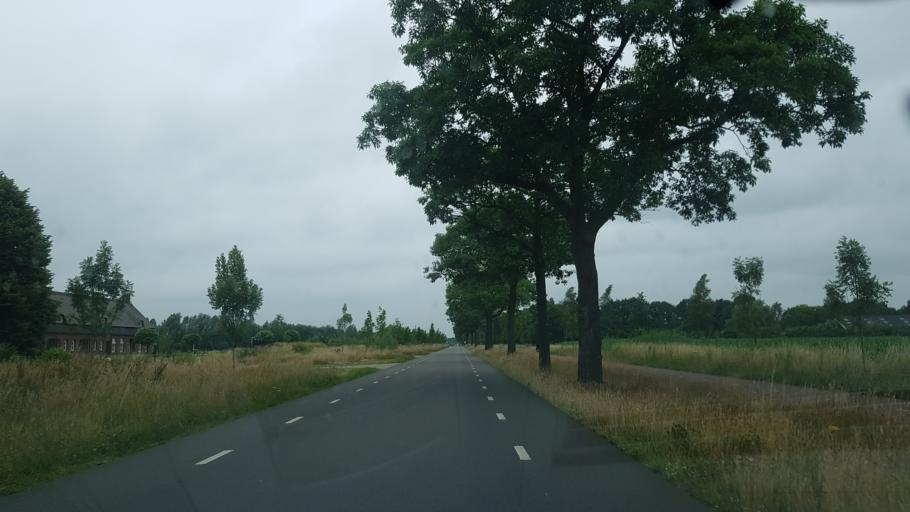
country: NL
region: North Brabant
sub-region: Gemeente Son en Breugel
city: Son
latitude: 51.5387
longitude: 5.4861
